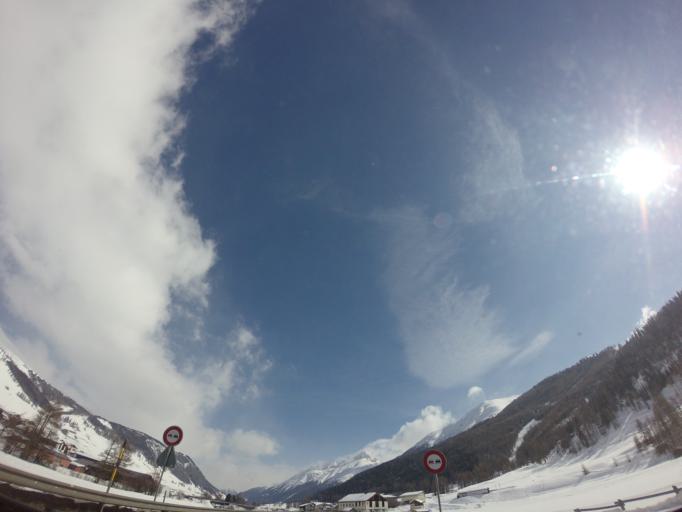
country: CH
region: Grisons
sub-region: Maloja District
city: Zuoz
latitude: 46.5953
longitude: 9.9606
